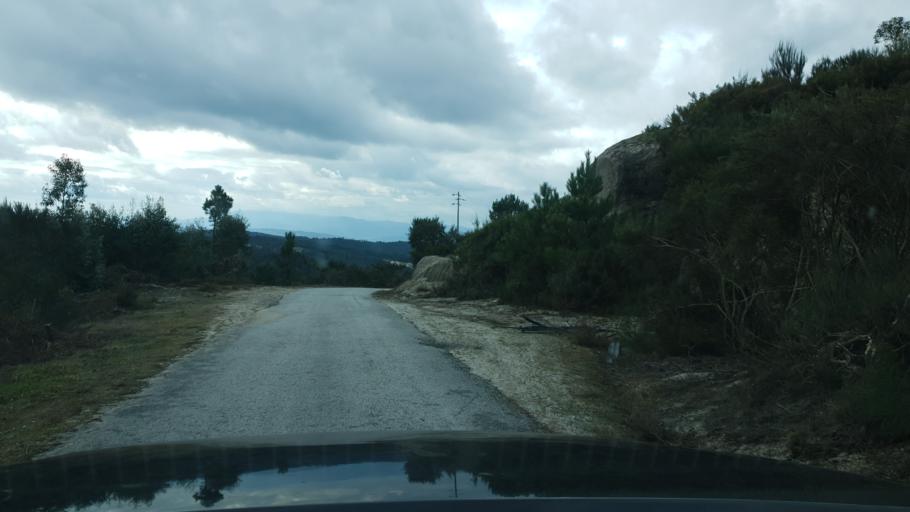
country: PT
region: Viseu
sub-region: Castro Daire
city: Castro Daire
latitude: 40.8723
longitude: -7.9875
